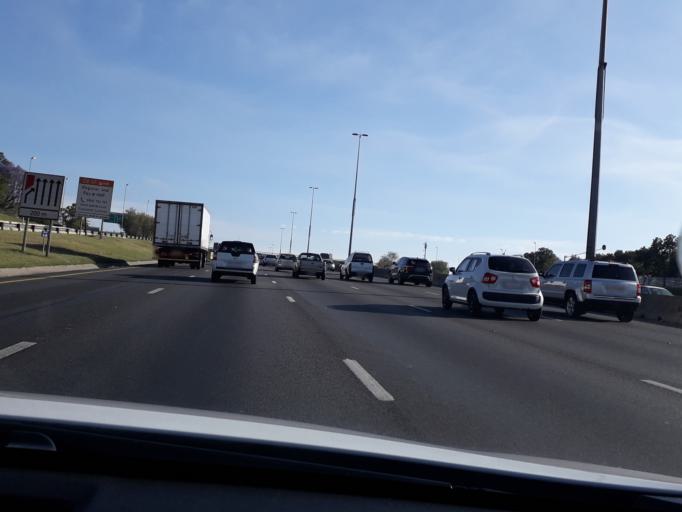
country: ZA
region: Gauteng
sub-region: City of Johannesburg Metropolitan Municipality
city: Midrand
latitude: -25.9838
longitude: 28.1250
